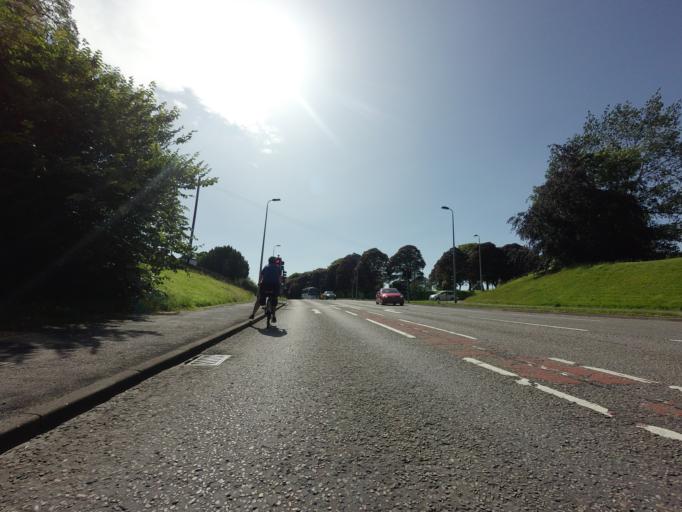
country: GB
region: Scotland
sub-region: Highland
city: Inverness
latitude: 57.4730
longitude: -4.2077
